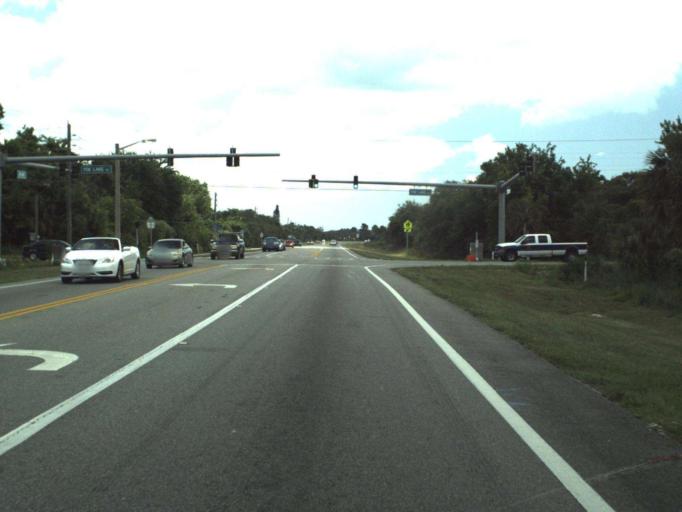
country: US
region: Florida
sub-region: Brevard County
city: Titusville
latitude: 28.5849
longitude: -80.8470
